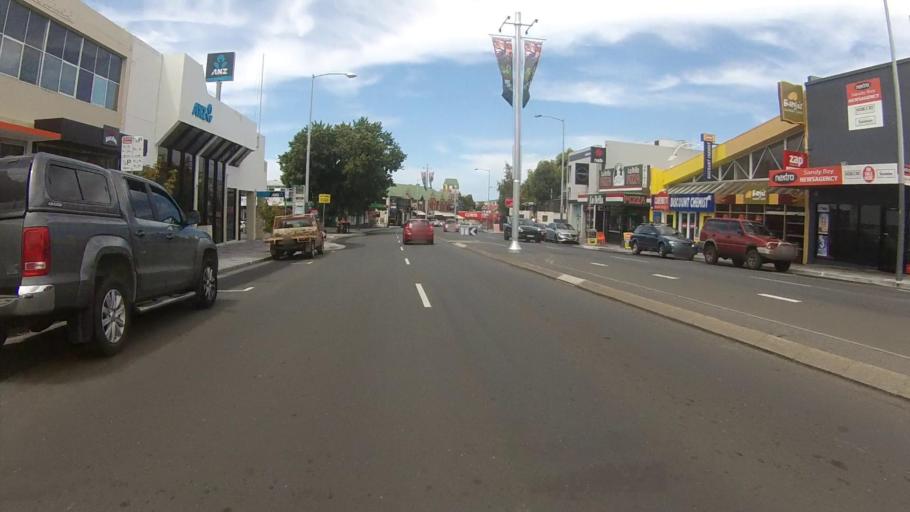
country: AU
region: Tasmania
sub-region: Hobart
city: Sandy Bay
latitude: -42.8948
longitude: 147.3269
